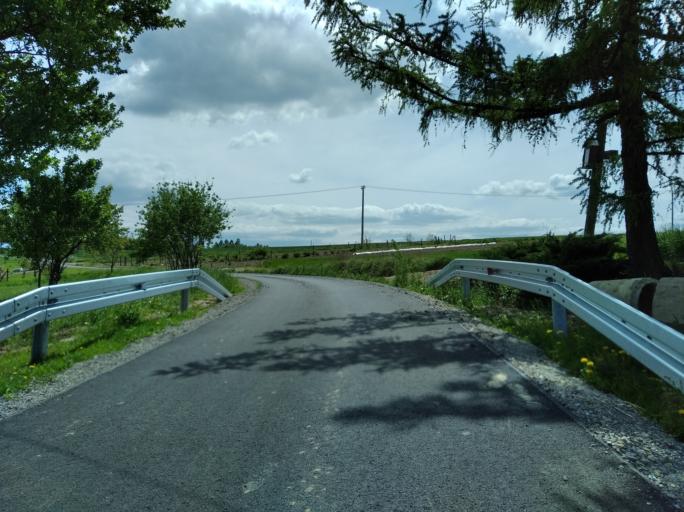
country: PL
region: Subcarpathian Voivodeship
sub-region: Powiat ropczycko-sedziszowski
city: Wielopole Skrzynskie
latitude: 49.9094
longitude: 21.5991
